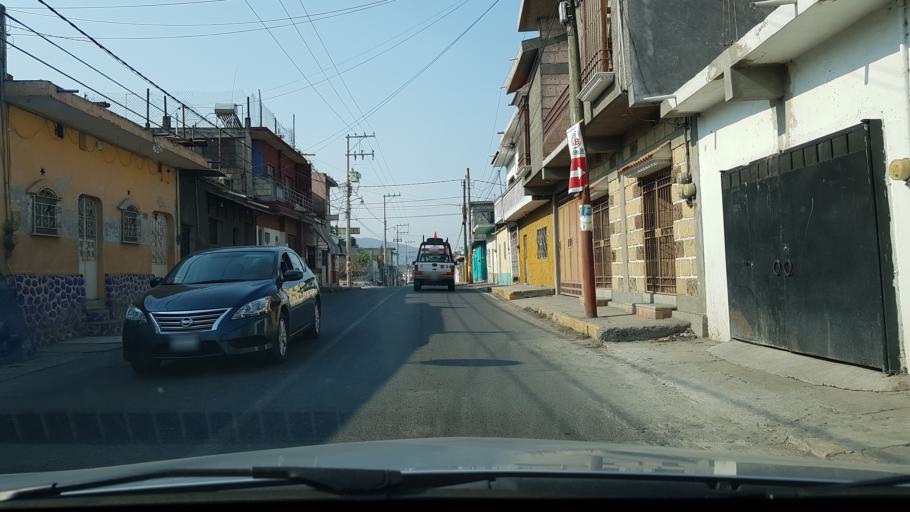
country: MX
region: Morelos
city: Tlaquiltenango
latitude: 18.6348
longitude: -99.1618
